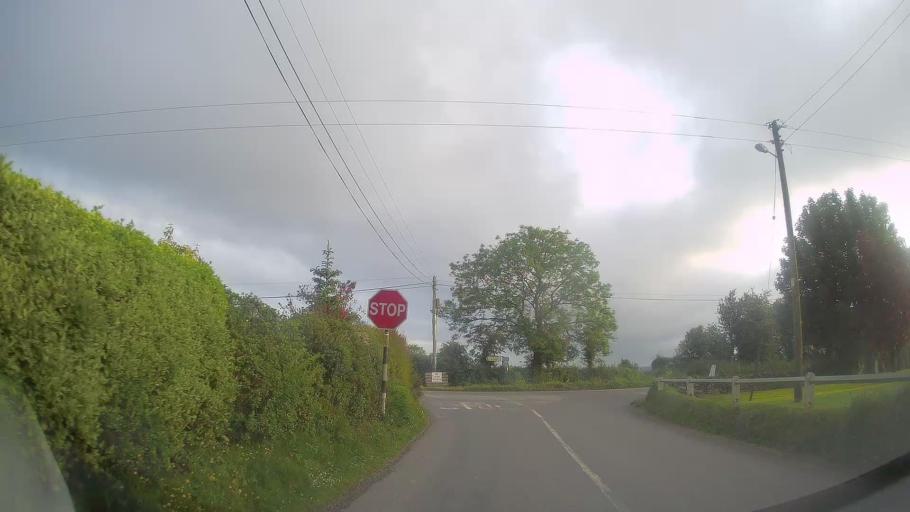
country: IE
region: Munster
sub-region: County Cork
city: Blarney
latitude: 51.9744
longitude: -8.5554
